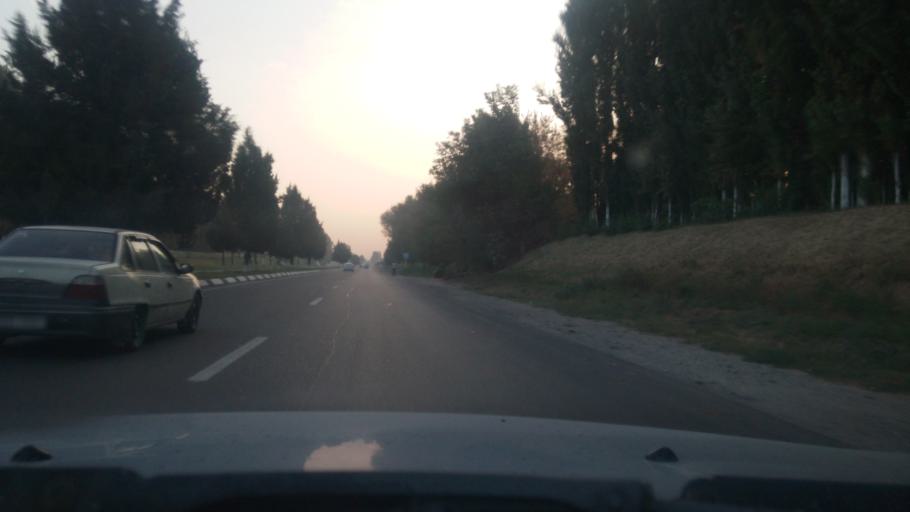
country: UZ
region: Toshkent
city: Amir Timur
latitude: 41.0686
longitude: 68.9213
